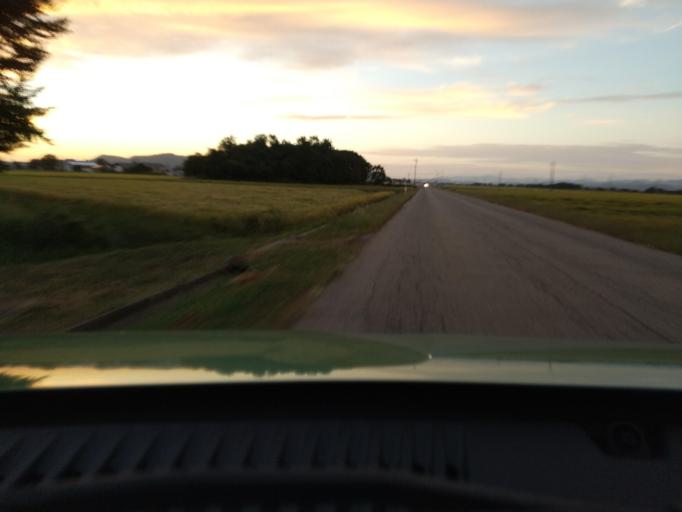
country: JP
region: Akita
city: Omagari
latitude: 39.4066
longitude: 140.5016
